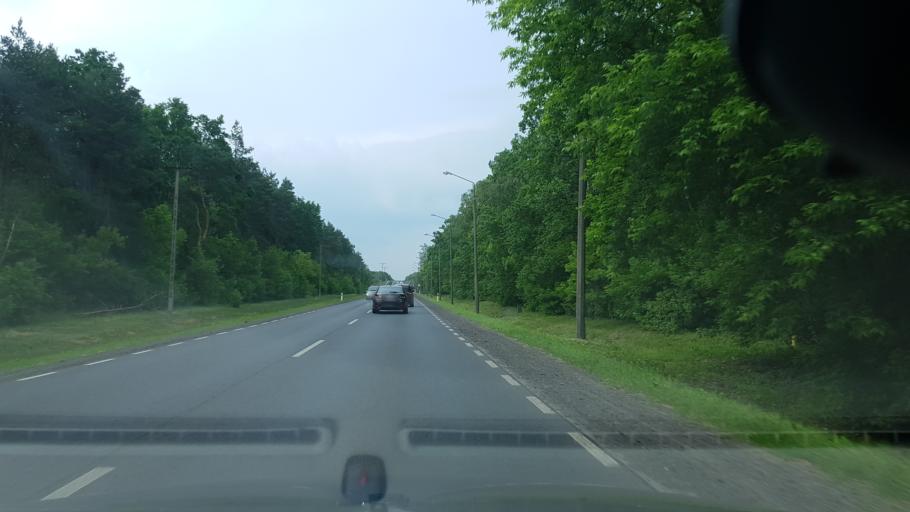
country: PL
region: Masovian Voivodeship
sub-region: Powiat legionowski
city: Michalow-Reginow
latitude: 52.4319
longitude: 20.9850
